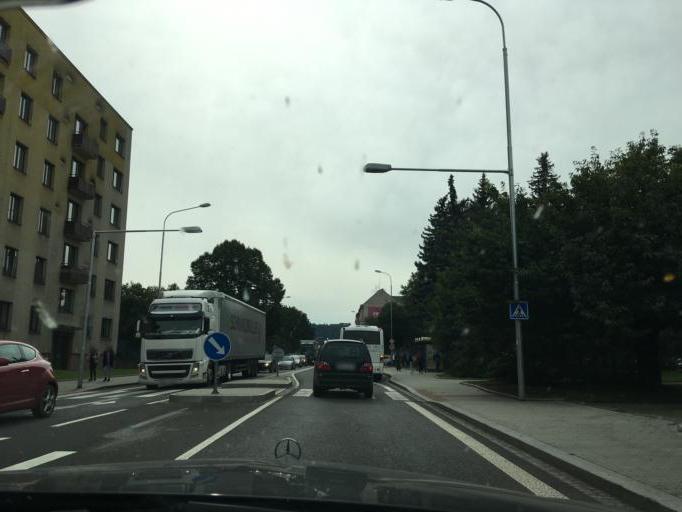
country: CZ
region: Kralovehradecky
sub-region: Okres Nachod
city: Nachod
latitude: 50.4139
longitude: 16.1660
